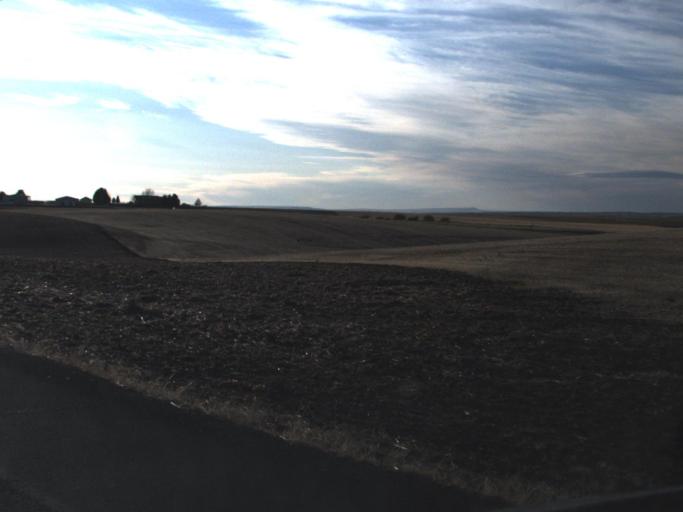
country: US
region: Washington
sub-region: Walla Walla County
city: Walla Walla East
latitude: 46.1091
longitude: -118.2316
